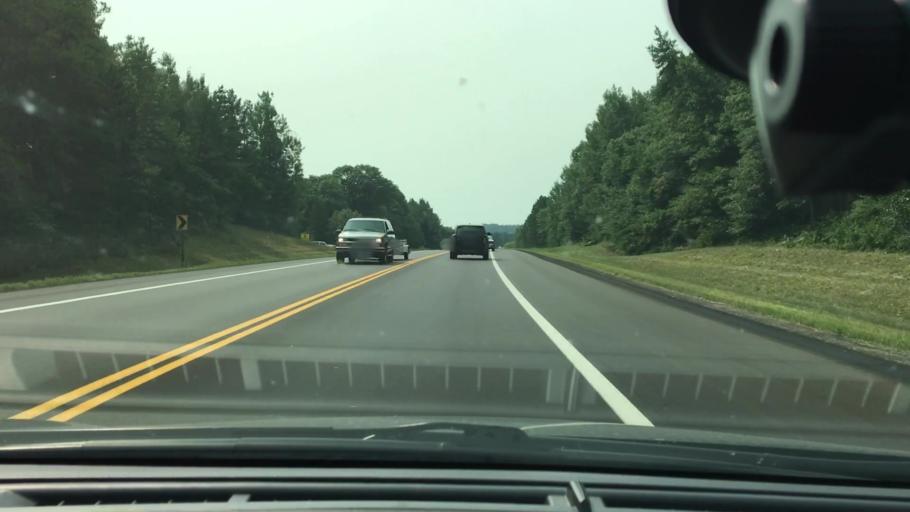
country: US
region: Minnesota
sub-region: Crow Wing County
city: Brainerd
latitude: 46.4109
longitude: -94.1760
